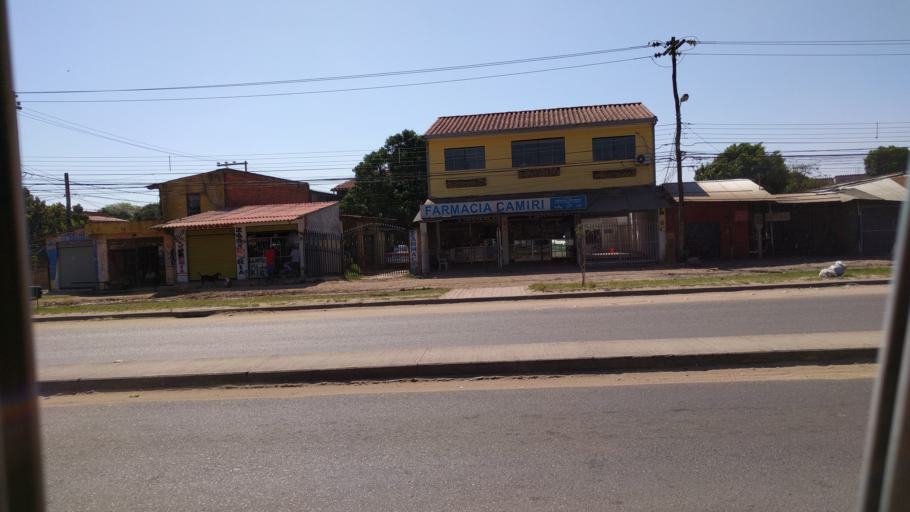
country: BO
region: Santa Cruz
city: Santa Cruz de la Sierra
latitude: -17.7683
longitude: -63.1166
